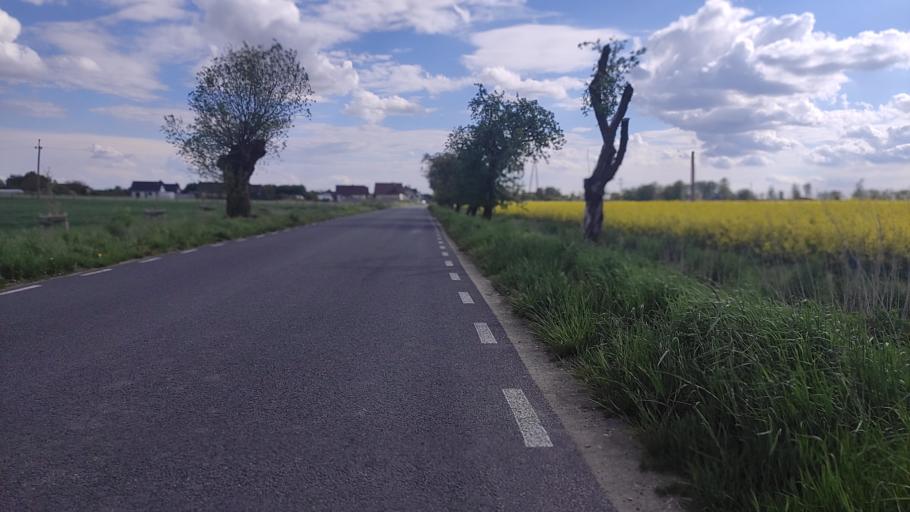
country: PL
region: Greater Poland Voivodeship
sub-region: Powiat poznanski
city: Kostrzyn
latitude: 52.4080
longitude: 17.1666
